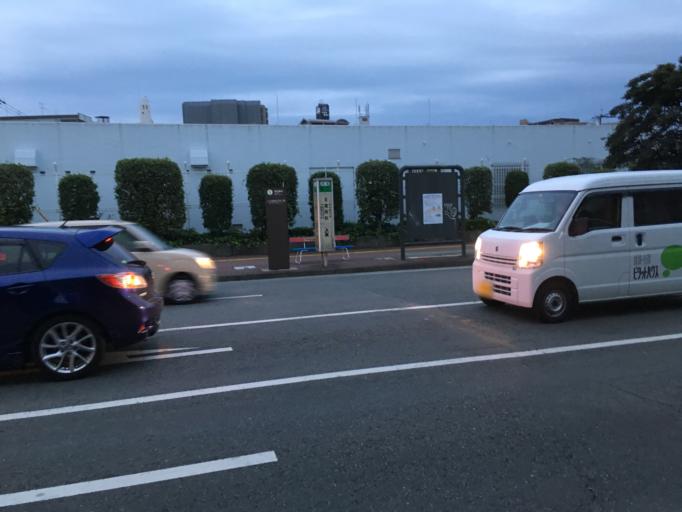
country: JP
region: Kumamoto
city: Kumamoto
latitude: 32.7971
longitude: 130.7277
